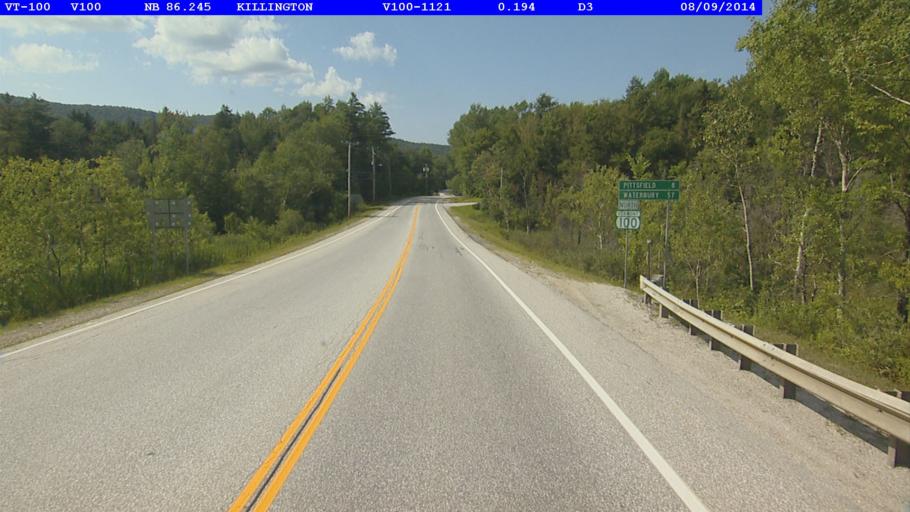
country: US
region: Vermont
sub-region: Rutland County
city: Rutland
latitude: 43.6704
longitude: -72.8058
